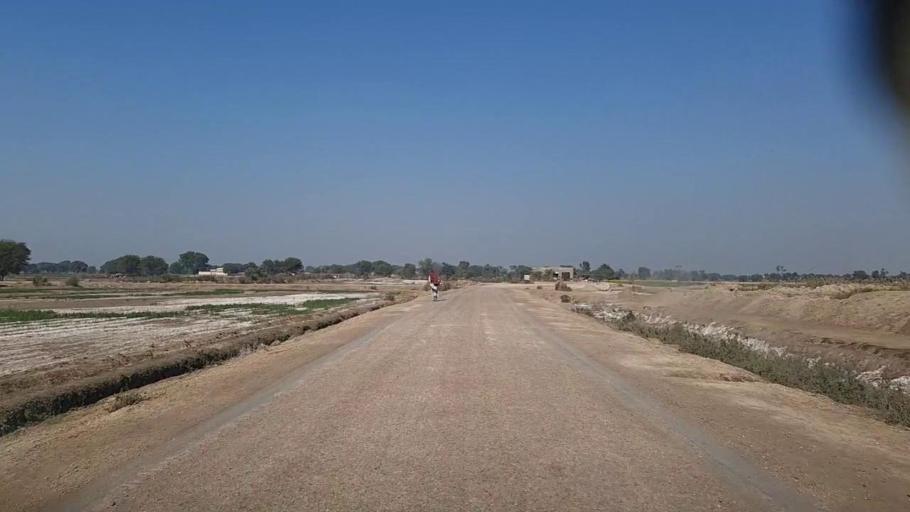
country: PK
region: Sindh
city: Khairpur
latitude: 27.9914
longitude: 69.8476
